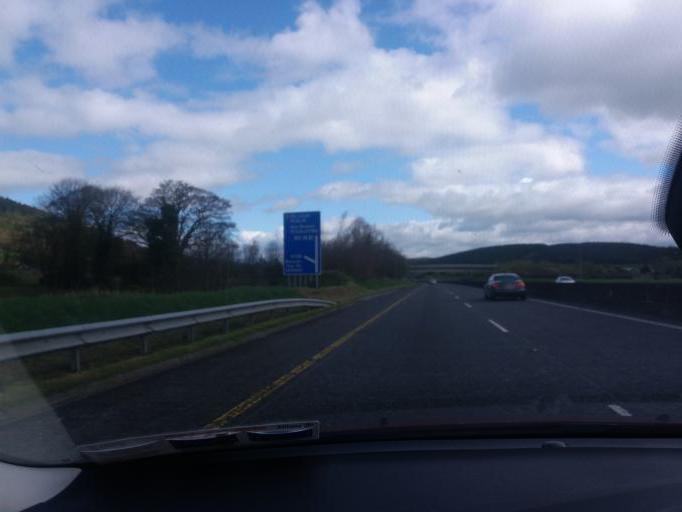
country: IE
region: Munster
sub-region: County Cork
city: Rathcormac
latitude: 52.1057
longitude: -8.2776
